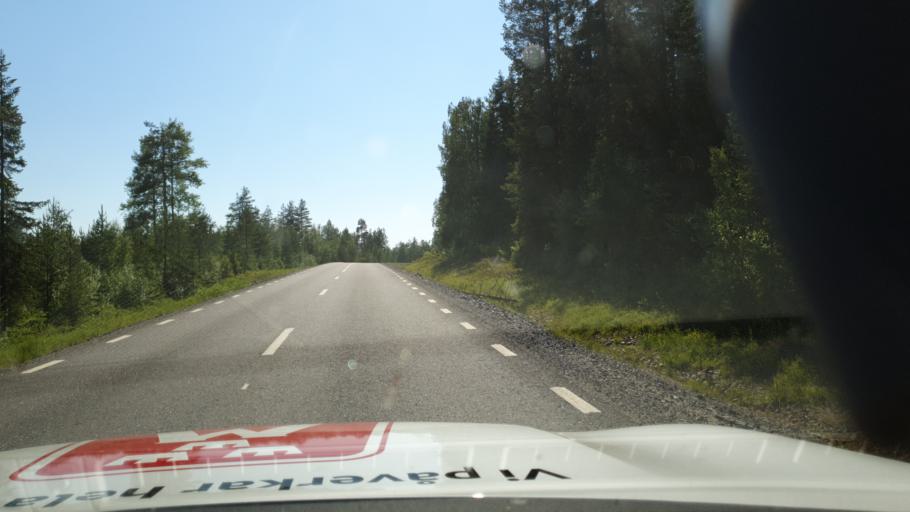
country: SE
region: Vaesterbotten
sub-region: Umea Kommun
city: Ersmark
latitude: 64.2528
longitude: 20.1555
